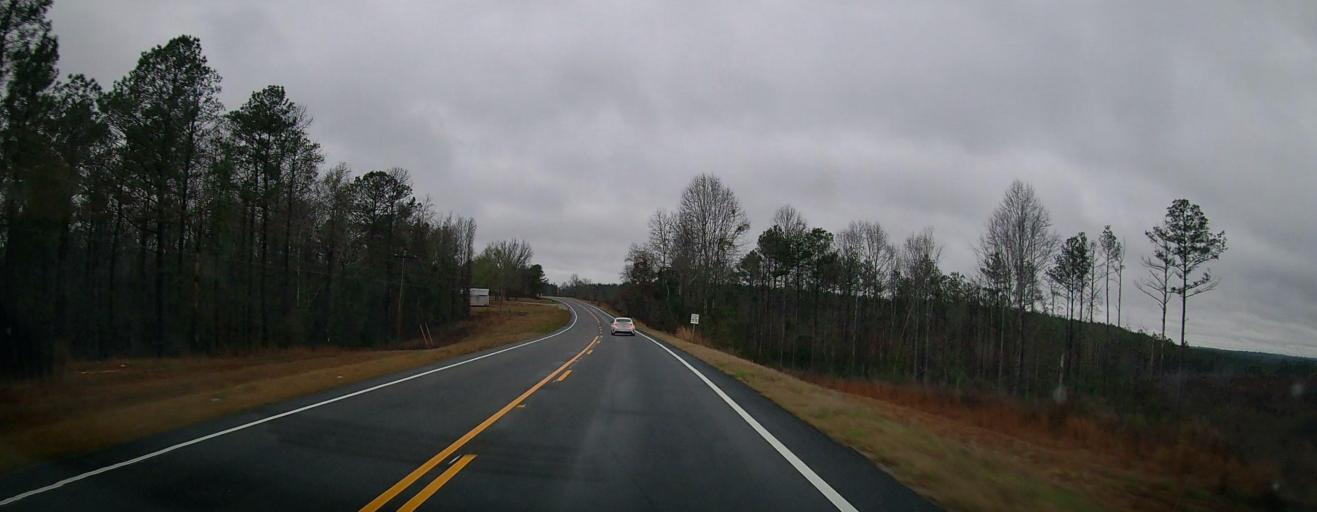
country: US
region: Alabama
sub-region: Chilton County
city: Clanton
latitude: 32.6976
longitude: -86.8017
